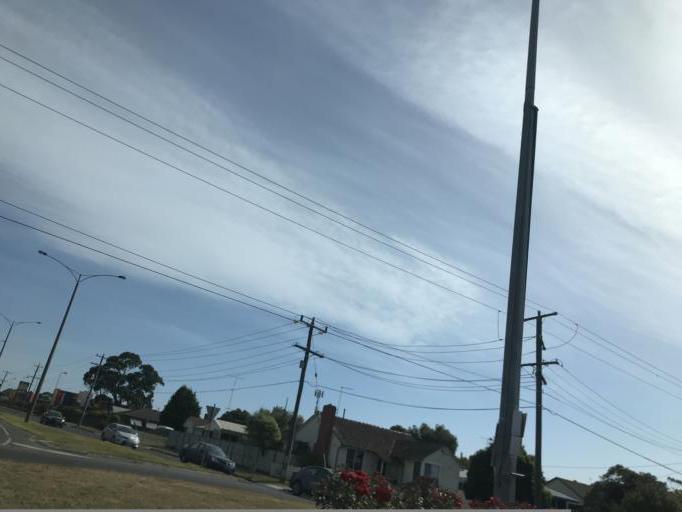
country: AU
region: Victoria
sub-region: Ballarat North
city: Newington
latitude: -37.5321
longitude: 143.8236
